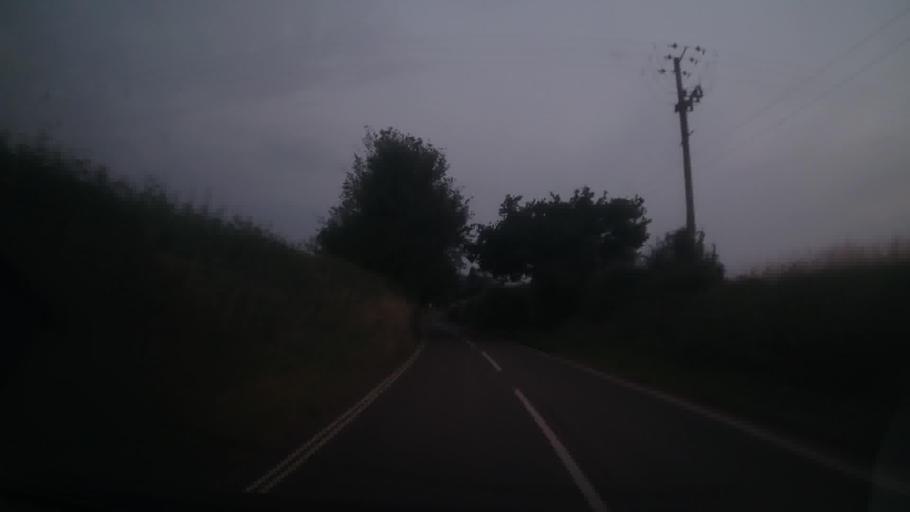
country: GB
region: England
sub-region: Leicestershire
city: Anstey
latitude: 52.6776
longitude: -1.2313
